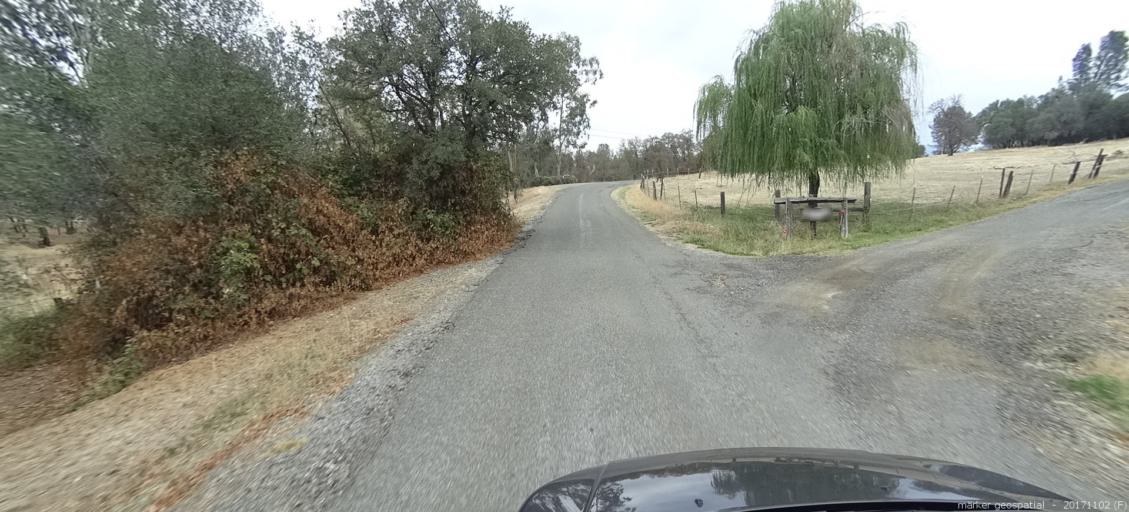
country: US
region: California
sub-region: Shasta County
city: Shasta Lake
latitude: 40.6586
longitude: -122.3151
